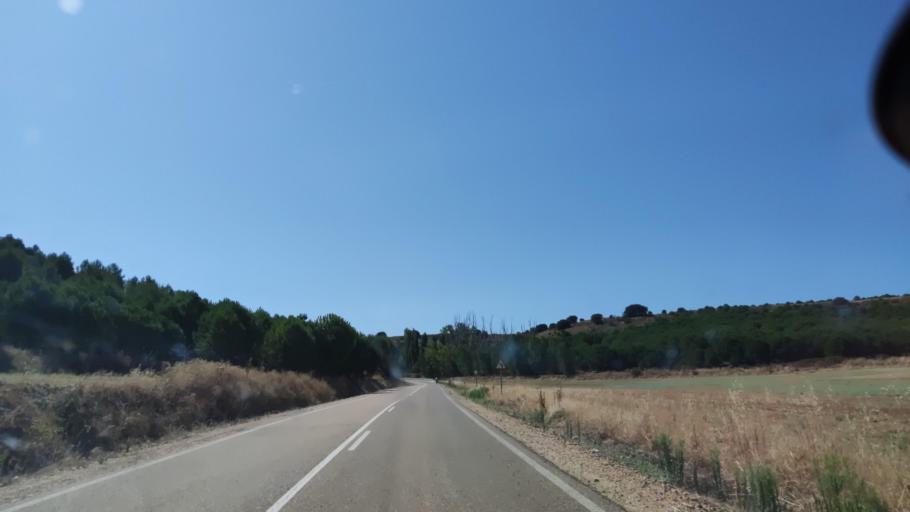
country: ES
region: Castille and Leon
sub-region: Provincia de Valladolid
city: Uruena
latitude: 41.7159
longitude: -5.1971
